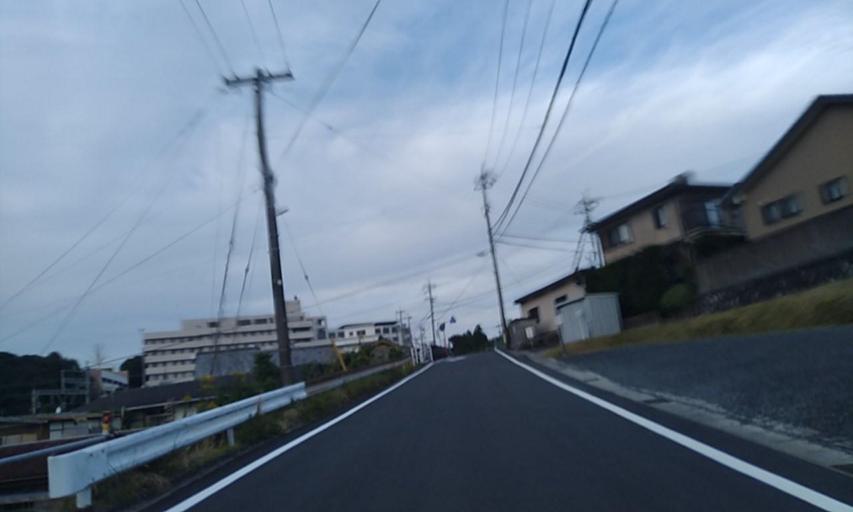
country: JP
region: Mie
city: Toba
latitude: 34.3324
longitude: 136.8195
